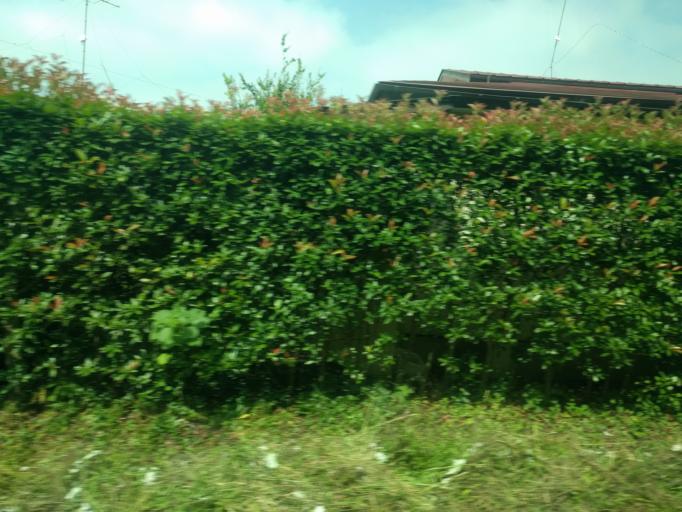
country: JP
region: Fukushima
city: Koriyama
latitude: 37.4554
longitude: 140.3412
